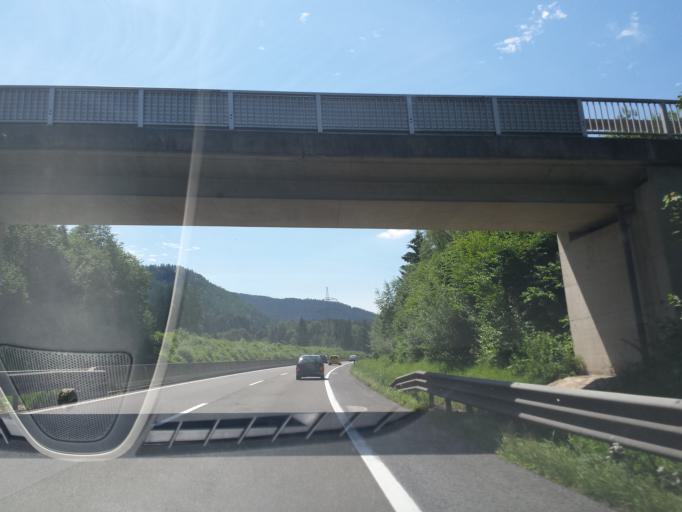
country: AT
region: Styria
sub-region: Politischer Bezirk Bruck-Muerzzuschlag
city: Krieglach
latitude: 47.5399
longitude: 15.5706
